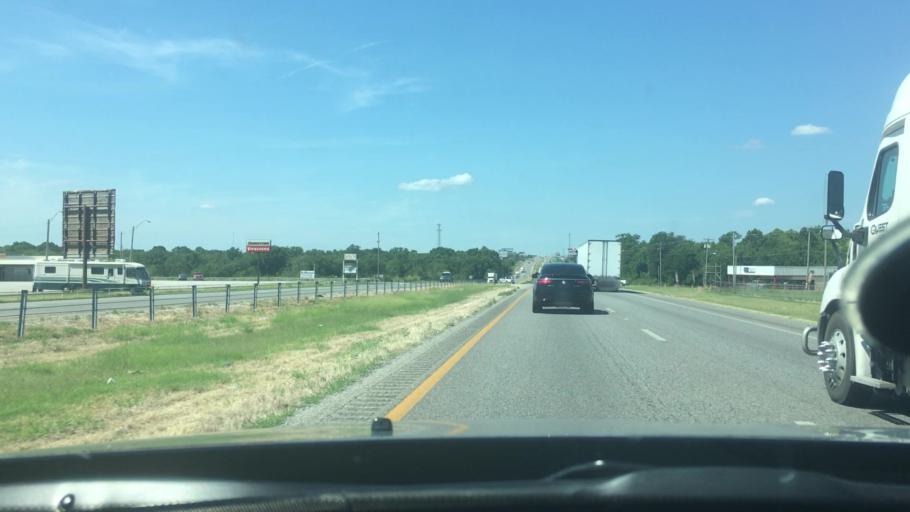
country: US
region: Oklahoma
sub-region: Bryan County
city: Calera
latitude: 33.9239
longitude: -96.4385
